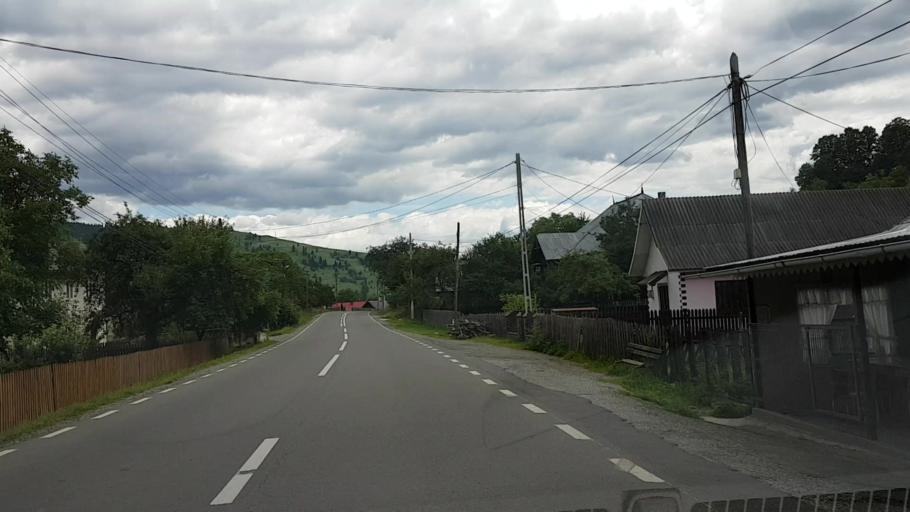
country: RO
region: Neamt
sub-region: Comuna Borca
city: Borca
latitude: 47.1915
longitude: 25.7695
